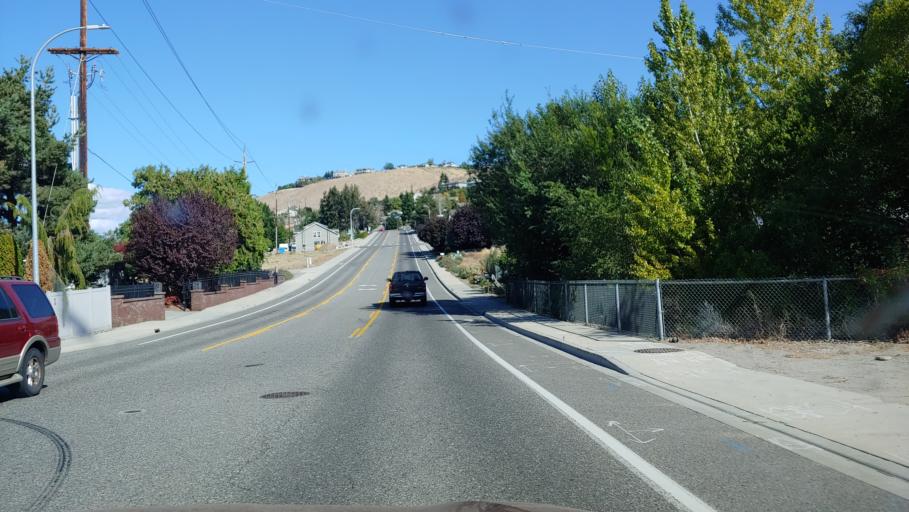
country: US
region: Washington
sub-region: Douglas County
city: East Wenatchee Bench
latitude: 47.4334
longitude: -120.2814
